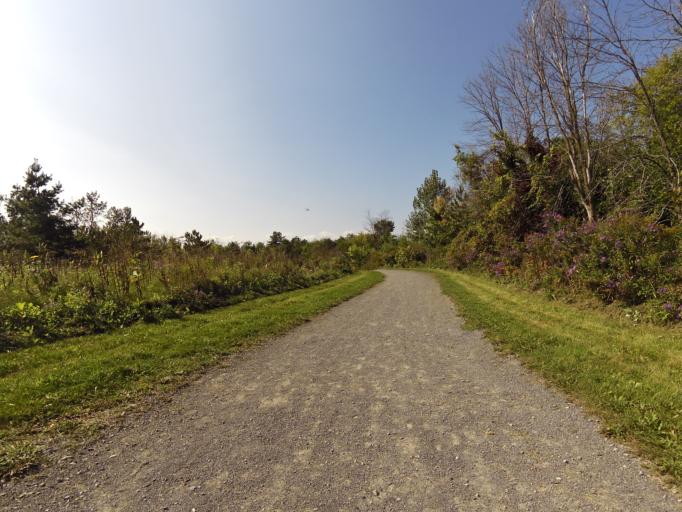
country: CA
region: Ontario
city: Bells Corners
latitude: 45.2624
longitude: -75.7303
